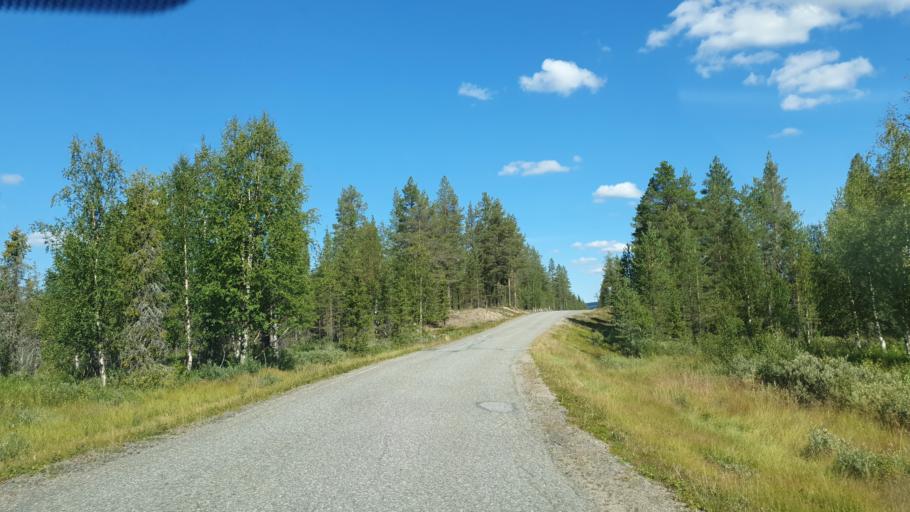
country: FI
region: Lapland
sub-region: Tunturi-Lappi
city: Muonio
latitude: 67.6905
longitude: 24.1082
